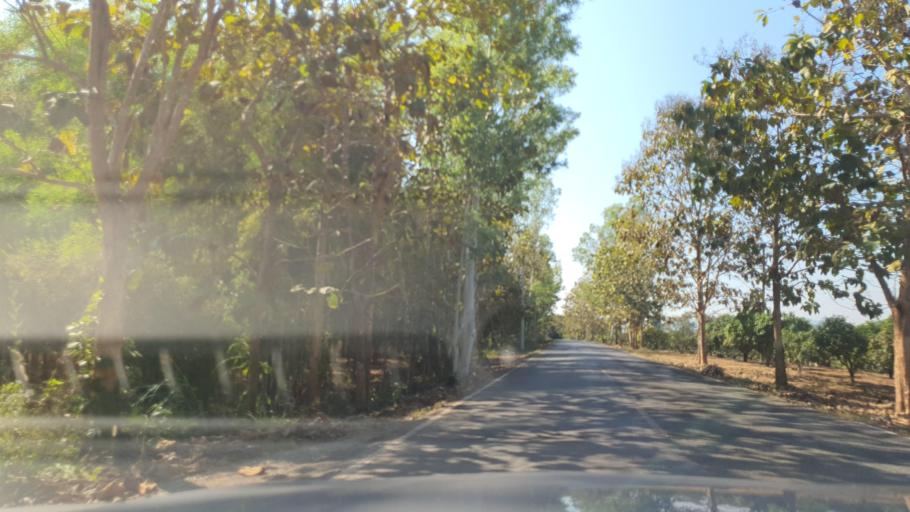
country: TH
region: Nan
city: Pua
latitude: 19.1198
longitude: 100.9144
